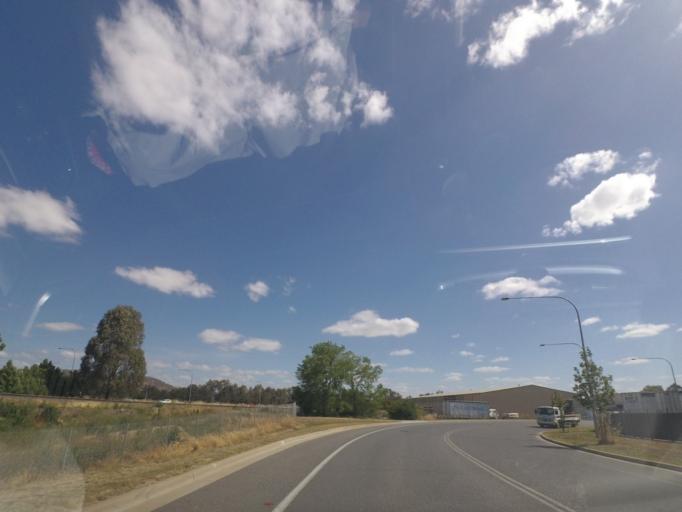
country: AU
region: New South Wales
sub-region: Albury Municipality
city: South Albury
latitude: -36.0934
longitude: 146.9218
